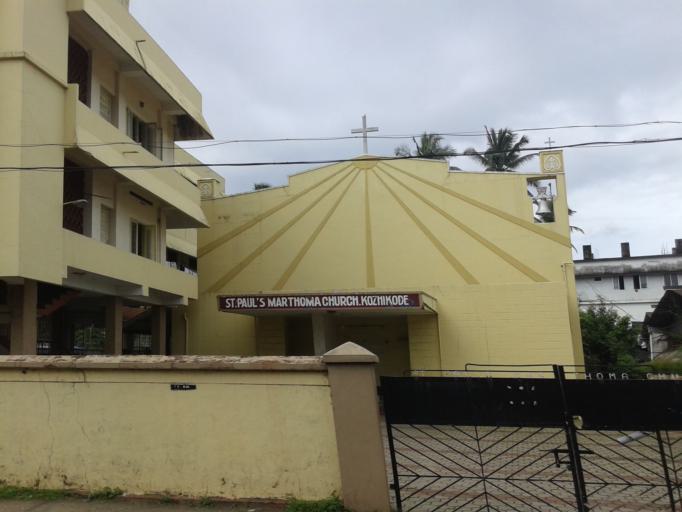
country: IN
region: Kerala
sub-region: Kozhikode
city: Kozhikode
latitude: 11.2582
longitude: 75.7777
